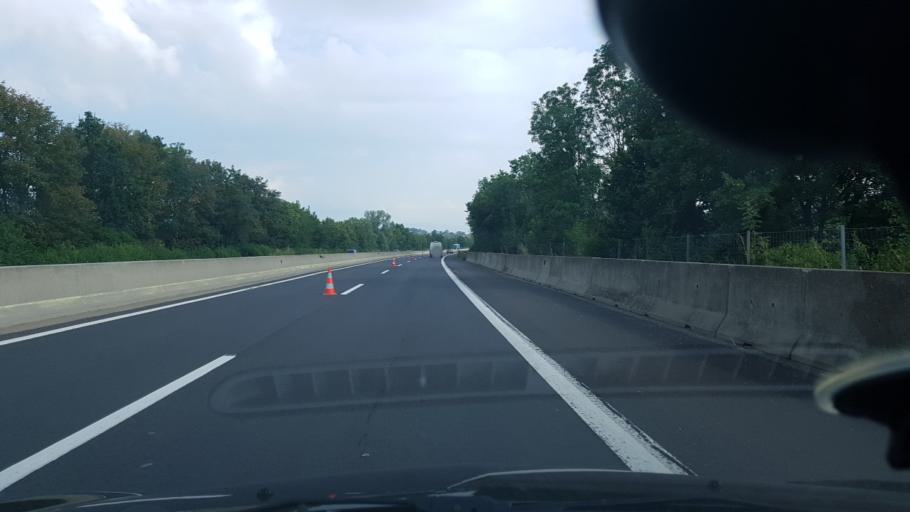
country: AT
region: Styria
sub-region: Politischer Bezirk Hartberg-Fuerstenfeld
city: Sebersdorf
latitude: 47.2032
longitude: 15.9905
